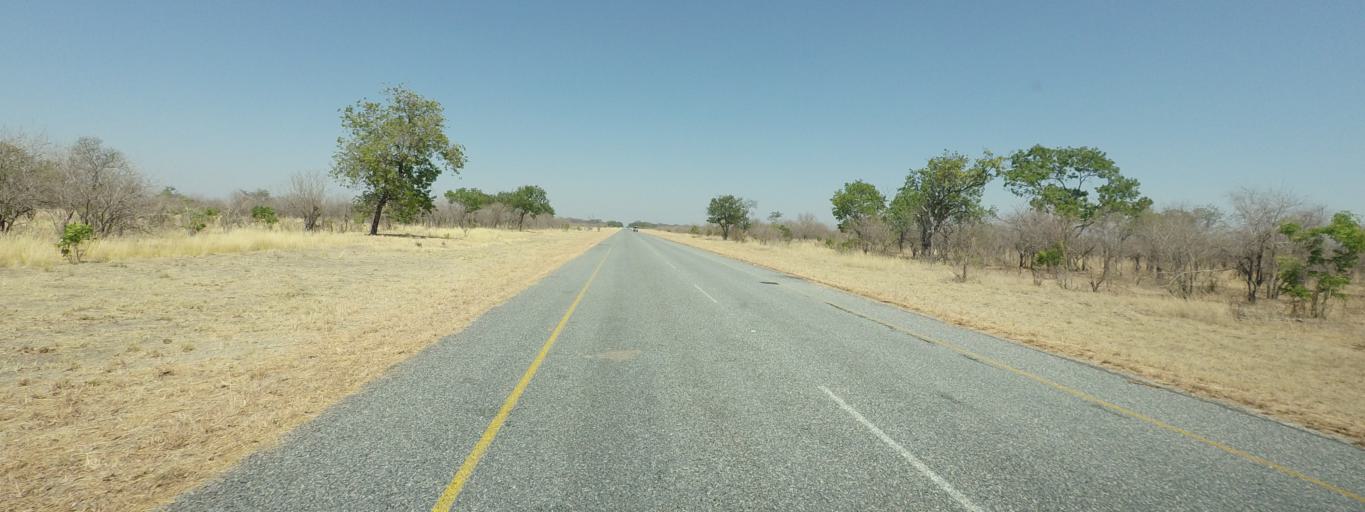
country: BW
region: North West
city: Kasane
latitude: -17.9219
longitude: 24.9386
